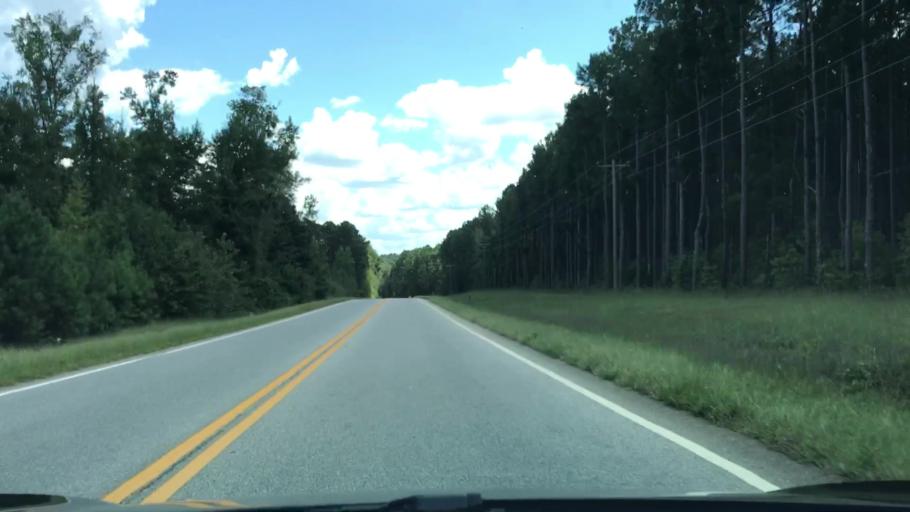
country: US
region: Georgia
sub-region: Greene County
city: Greensboro
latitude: 33.6766
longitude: -83.2683
